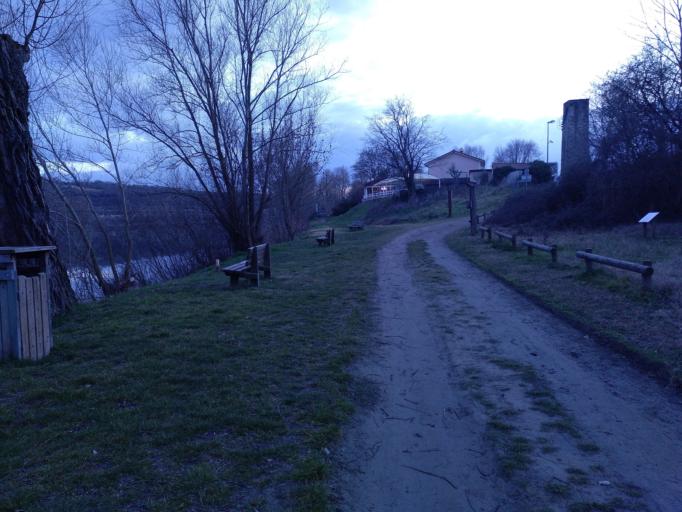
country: FR
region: Rhone-Alpes
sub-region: Departement du Rhone
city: Grigny
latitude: 45.6140
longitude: 4.8009
